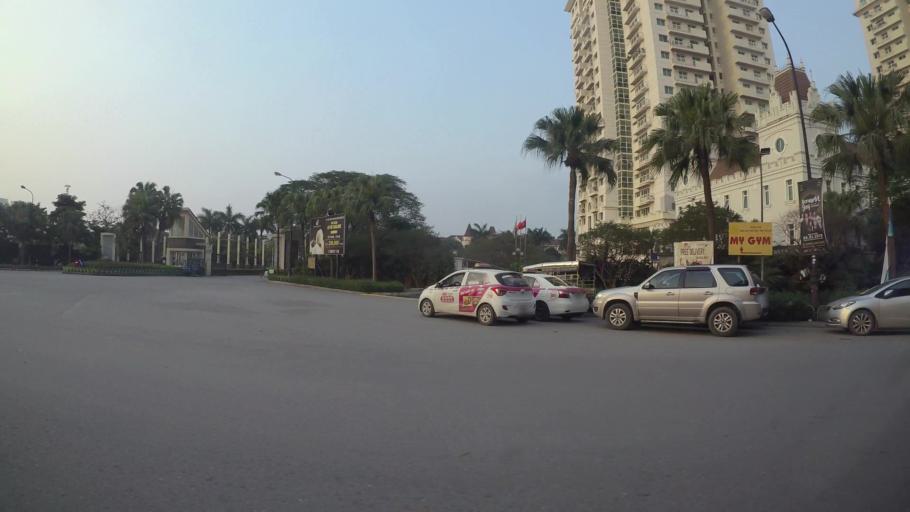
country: VN
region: Ha Noi
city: Tay Ho
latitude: 21.0737
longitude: 105.8003
